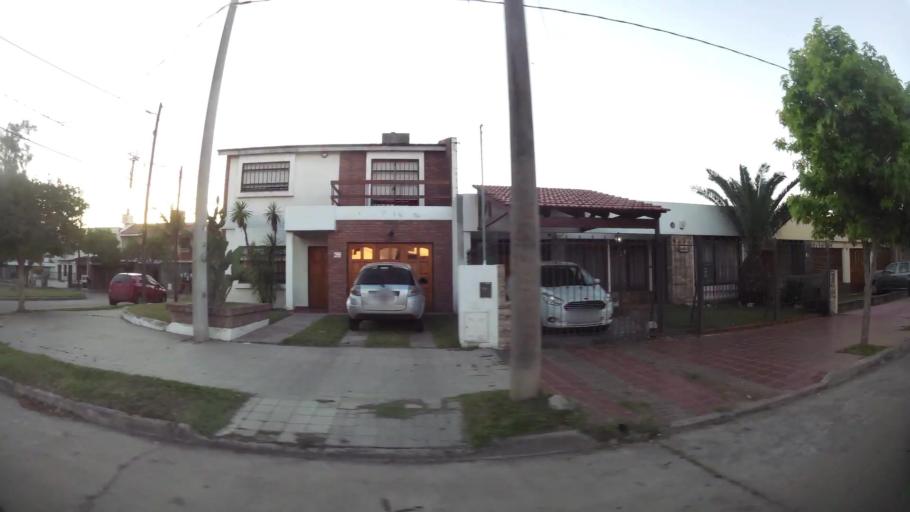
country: AR
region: Cordoba
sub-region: Departamento de Capital
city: Cordoba
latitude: -31.3777
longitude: -64.2174
